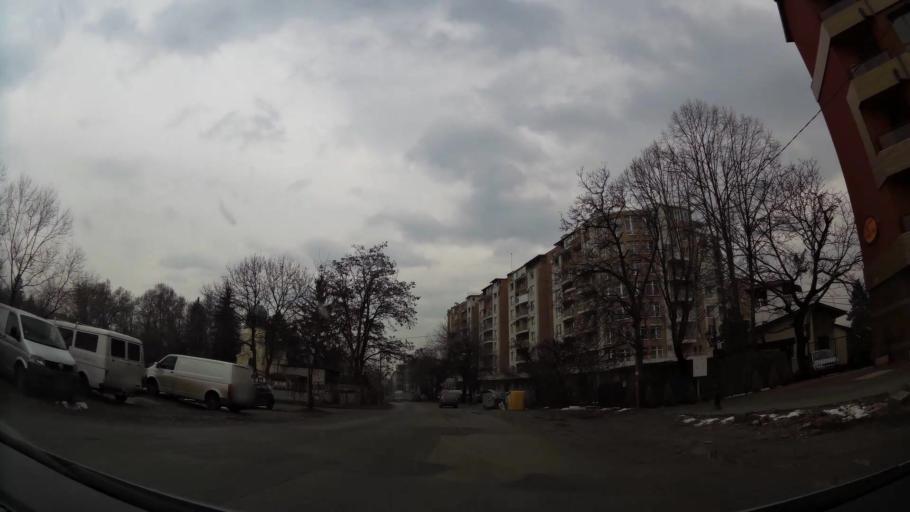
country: BG
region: Sofia-Capital
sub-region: Stolichna Obshtina
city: Sofia
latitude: 42.6639
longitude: 23.2468
